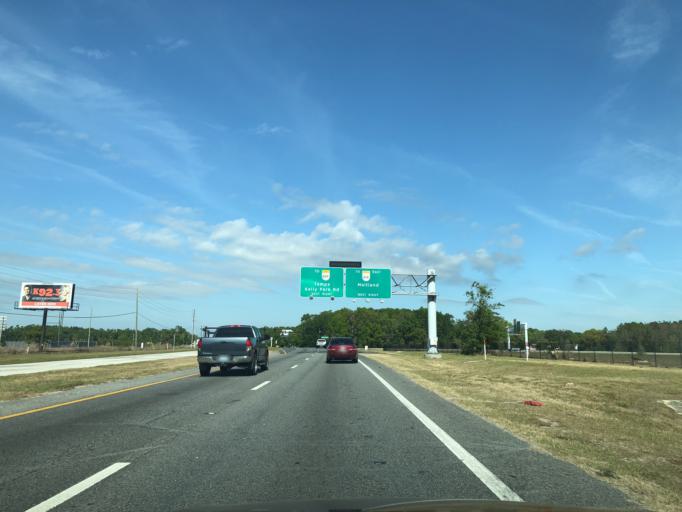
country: US
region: Florida
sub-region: Orange County
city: Apopka
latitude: 28.6956
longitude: -81.5607
